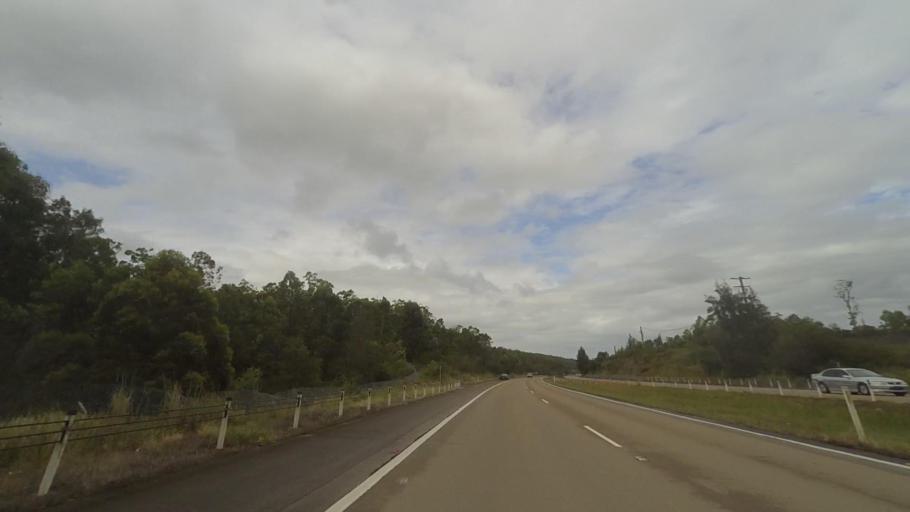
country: AU
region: New South Wales
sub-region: Port Stephens Shire
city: Medowie
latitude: -32.6238
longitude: 151.9482
